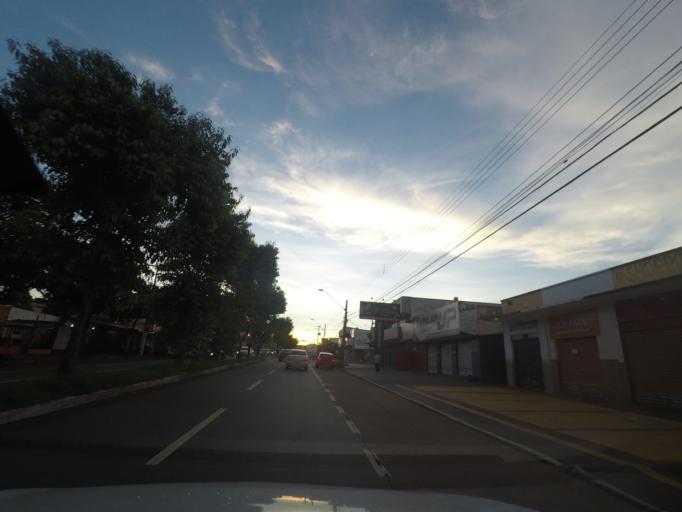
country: BR
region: Goias
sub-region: Goiania
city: Goiania
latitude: -16.6959
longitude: -49.2993
